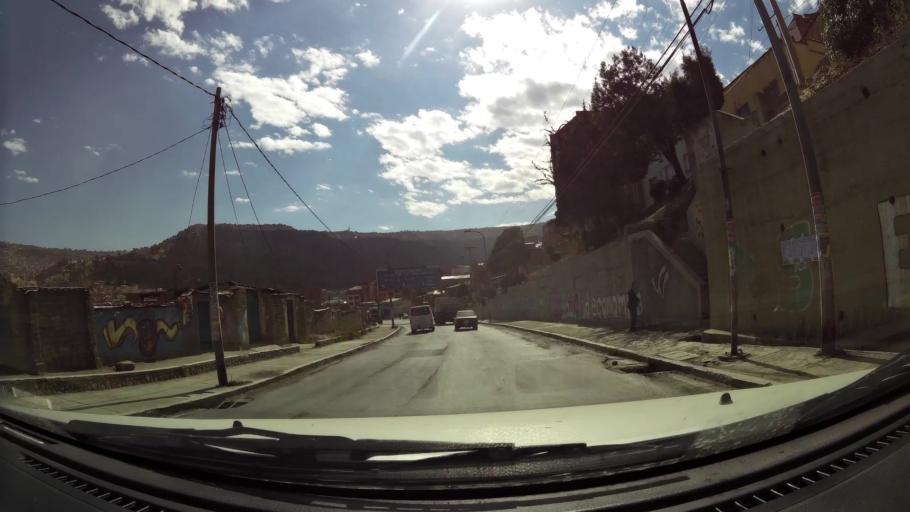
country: BO
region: La Paz
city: La Paz
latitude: -16.4844
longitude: -68.1421
